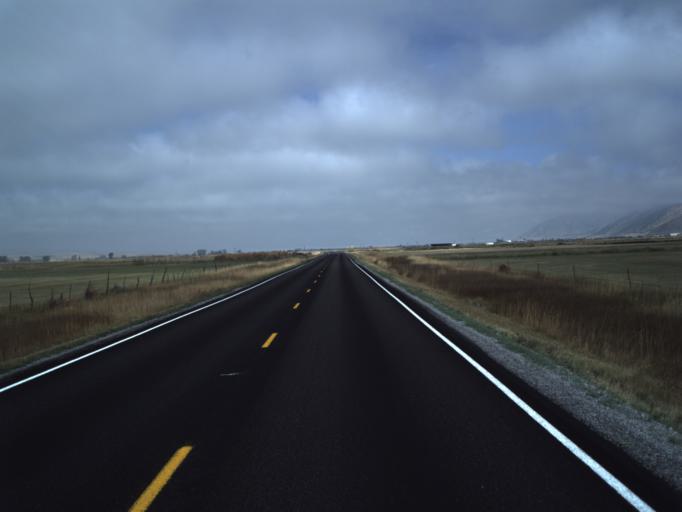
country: US
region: Utah
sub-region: Rich County
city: Randolph
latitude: 41.4977
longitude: -111.1219
